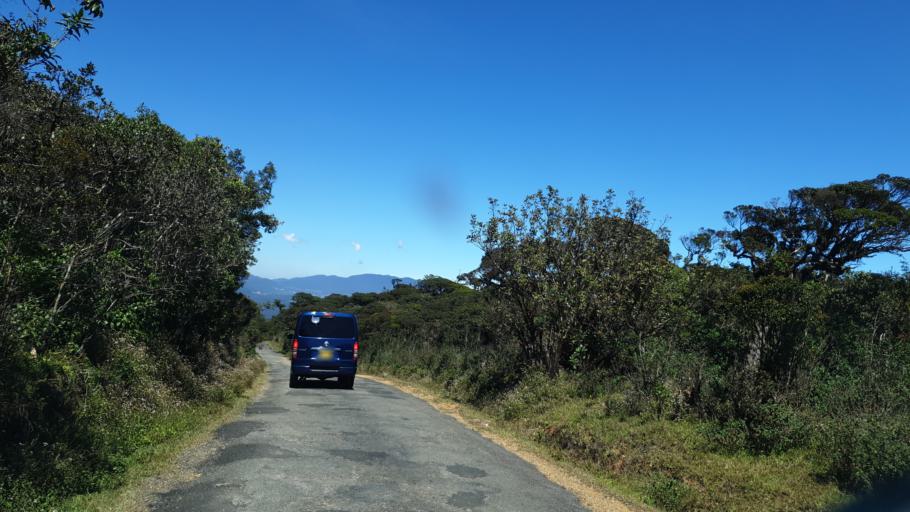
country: LK
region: Central
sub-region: Nuwara Eliya District
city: Nuwara Eliya
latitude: 6.8406
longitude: 80.8128
